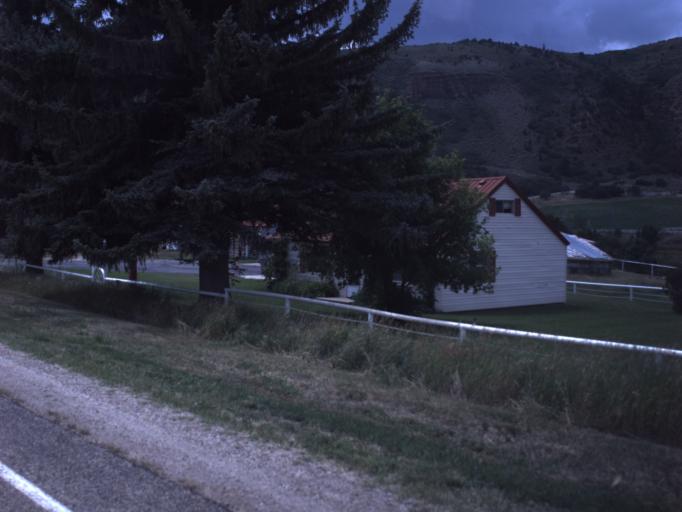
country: US
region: Utah
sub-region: Summit County
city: Francis
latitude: 40.4459
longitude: -110.8180
